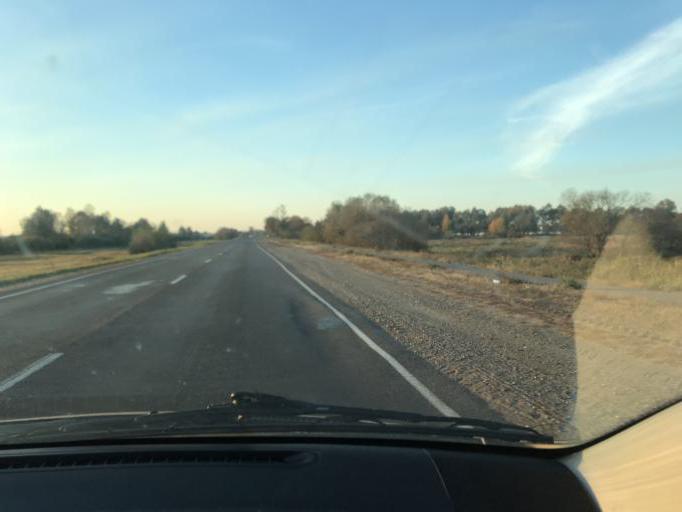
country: BY
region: Brest
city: Pinsk
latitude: 52.0879
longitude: 26.1319
